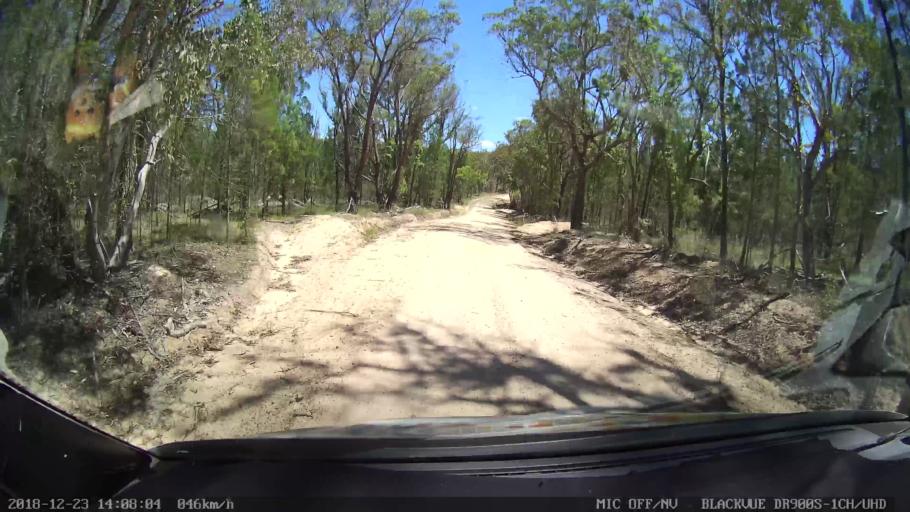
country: AU
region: New South Wales
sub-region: Tamworth Municipality
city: Manilla
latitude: -30.6400
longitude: 151.0700
